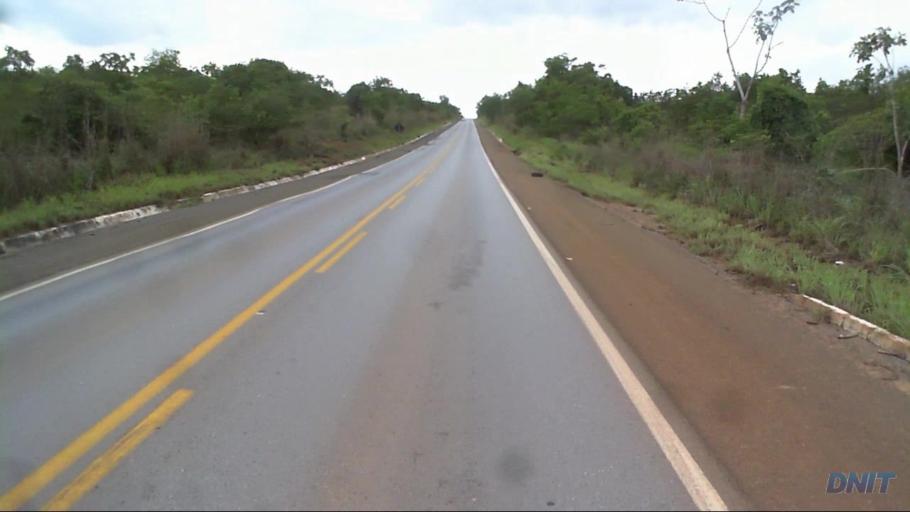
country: BR
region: Goias
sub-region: Uruacu
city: Uruacu
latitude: -14.7533
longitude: -49.0711
